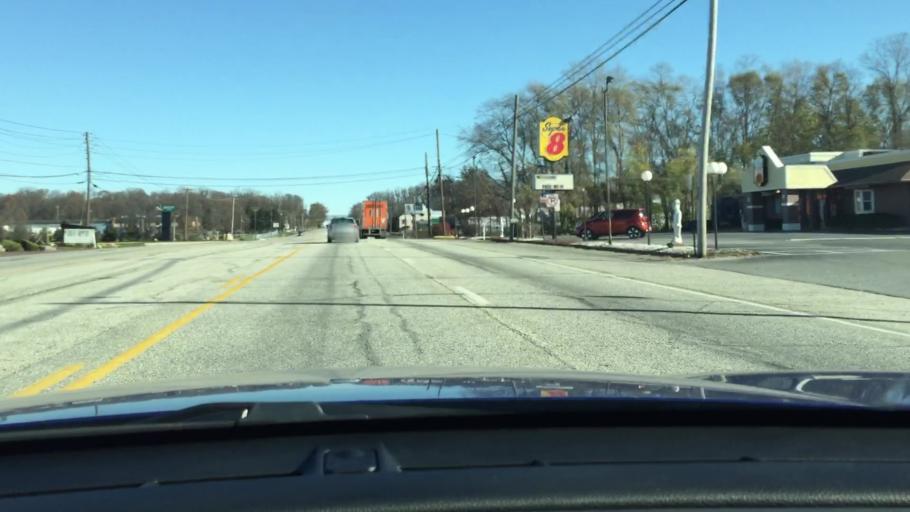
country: US
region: Pennsylvania
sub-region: Cumberland County
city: Schlusser
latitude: 40.2336
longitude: -77.1176
